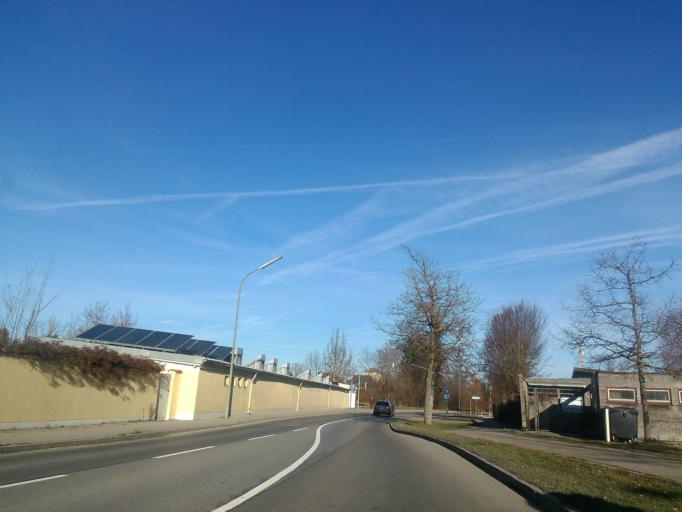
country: DE
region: Bavaria
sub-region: Swabia
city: Aichach
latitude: 48.4583
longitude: 11.1246
